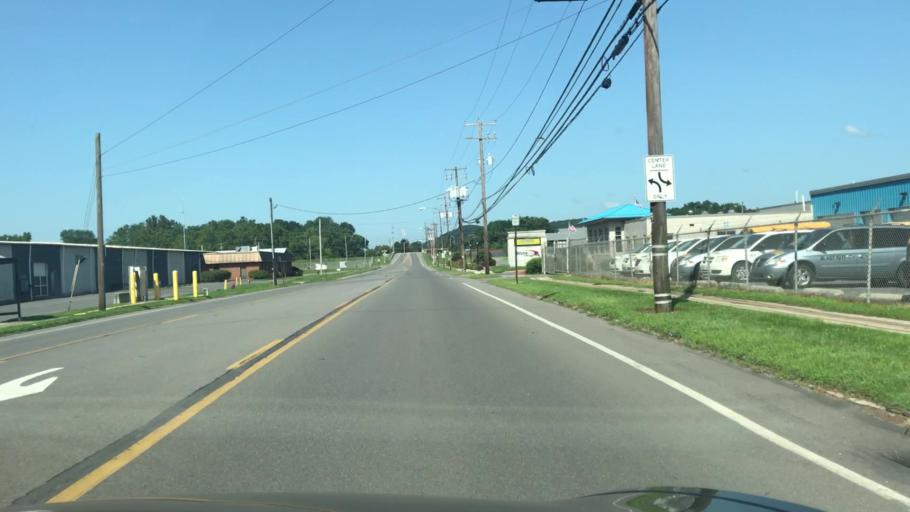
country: US
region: Pennsylvania
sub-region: Lycoming County
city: Duboistown
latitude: 41.2371
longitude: -77.0371
